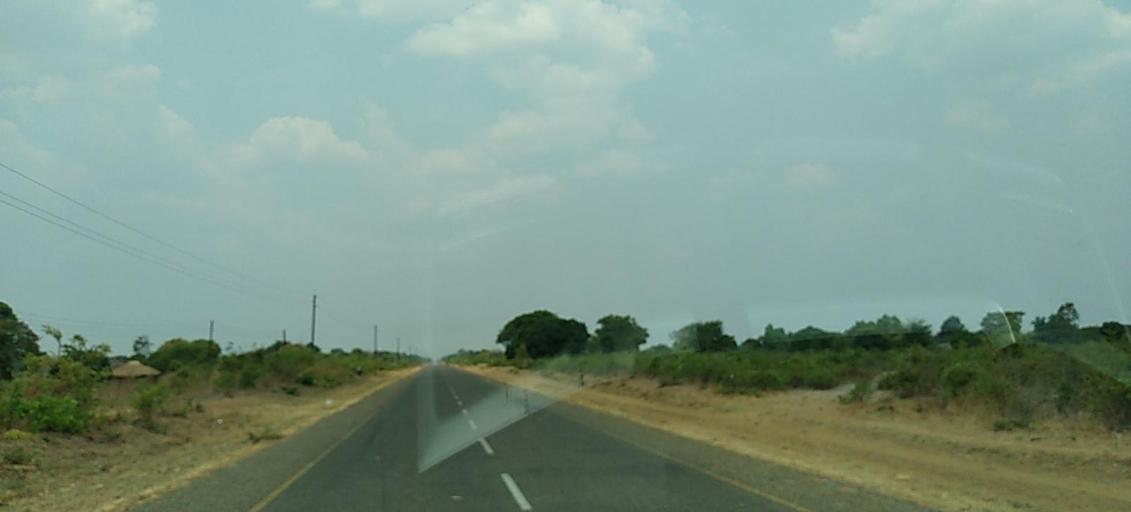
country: ZM
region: North-Western
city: Zambezi
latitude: -13.5512
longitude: 23.1262
